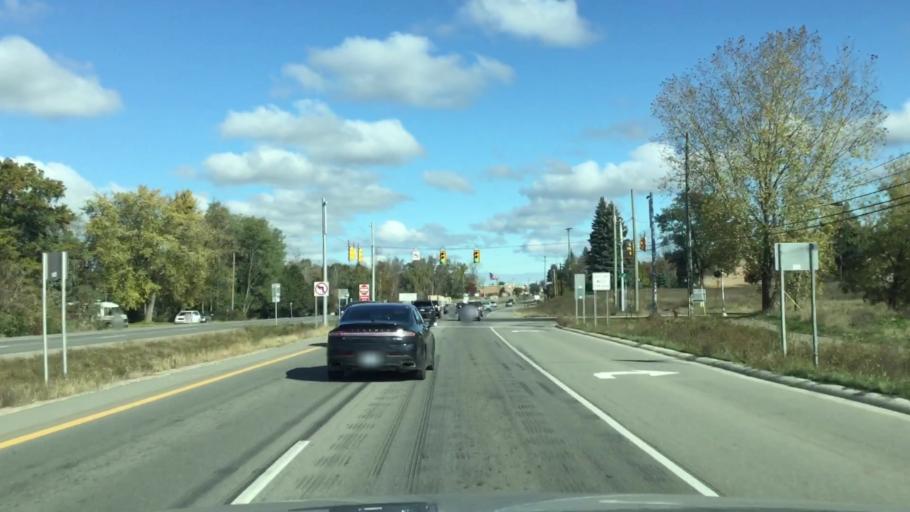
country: US
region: Michigan
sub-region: Oakland County
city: Lake Orion
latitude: 42.7548
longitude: -83.2462
